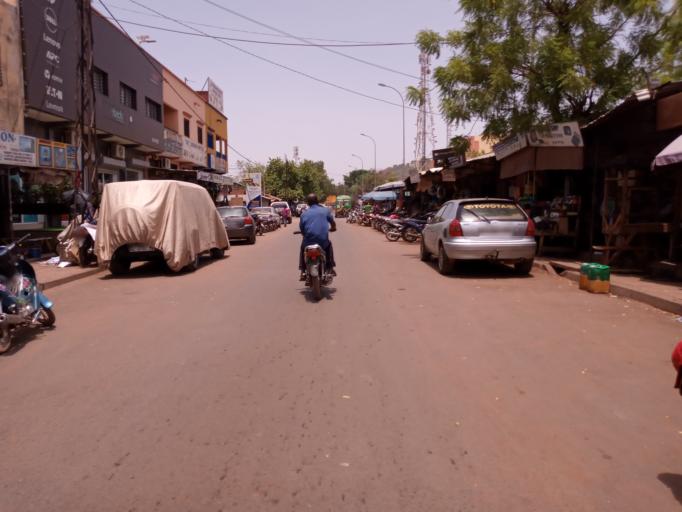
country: ML
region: Bamako
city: Bamako
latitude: 12.6416
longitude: -8.0010
